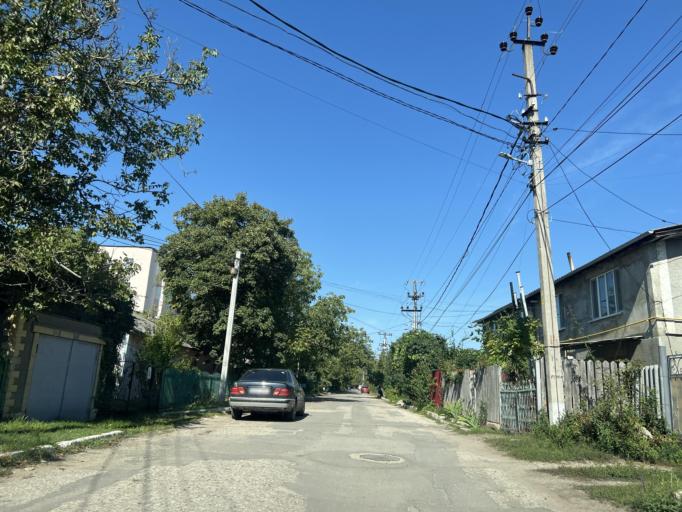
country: RO
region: Iasi
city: Ungheni-Prut
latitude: 47.1958
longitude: 27.7945
